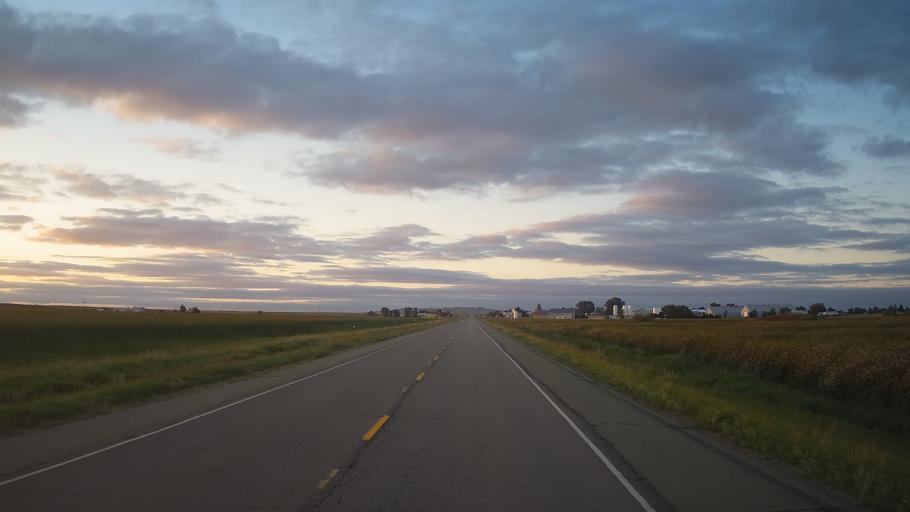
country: US
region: South Dakota
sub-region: Lyman County
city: Kennebec
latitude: 43.8702
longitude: -99.6061
